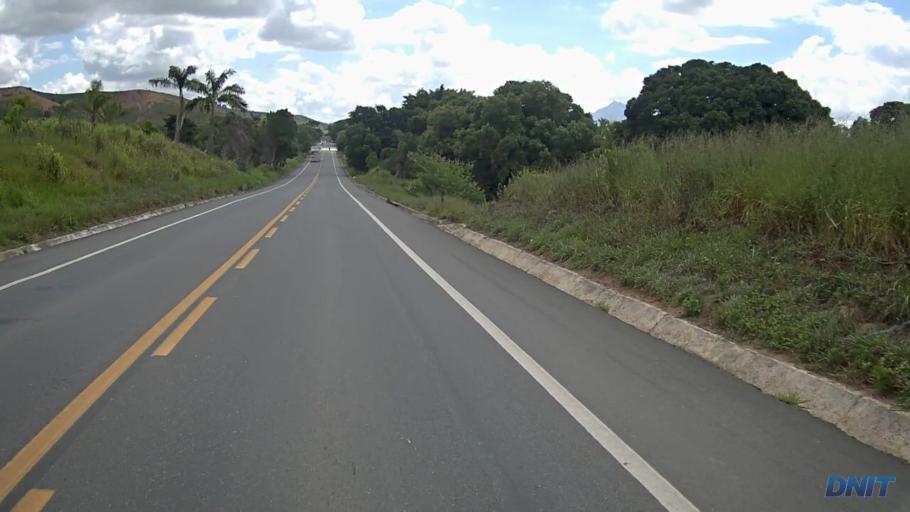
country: BR
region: Minas Gerais
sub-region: Governador Valadares
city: Governador Valadares
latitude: -18.9413
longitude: -42.0586
